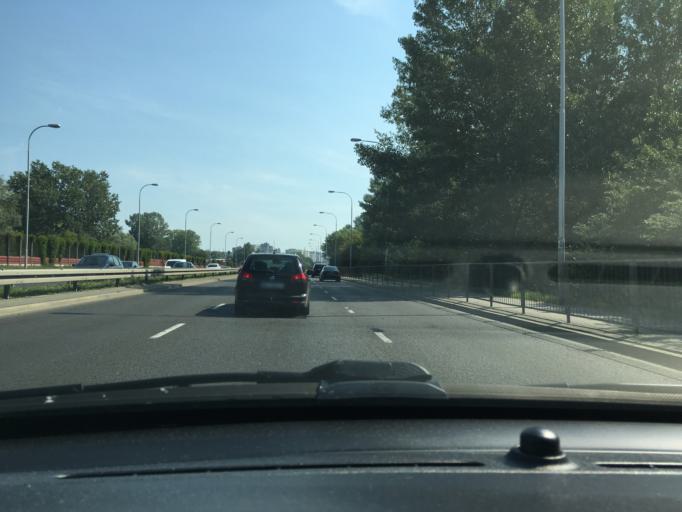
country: PL
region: Masovian Voivodeship
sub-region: Warszawa
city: Praga Poludnie
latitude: 52.2215
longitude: 21.0745
